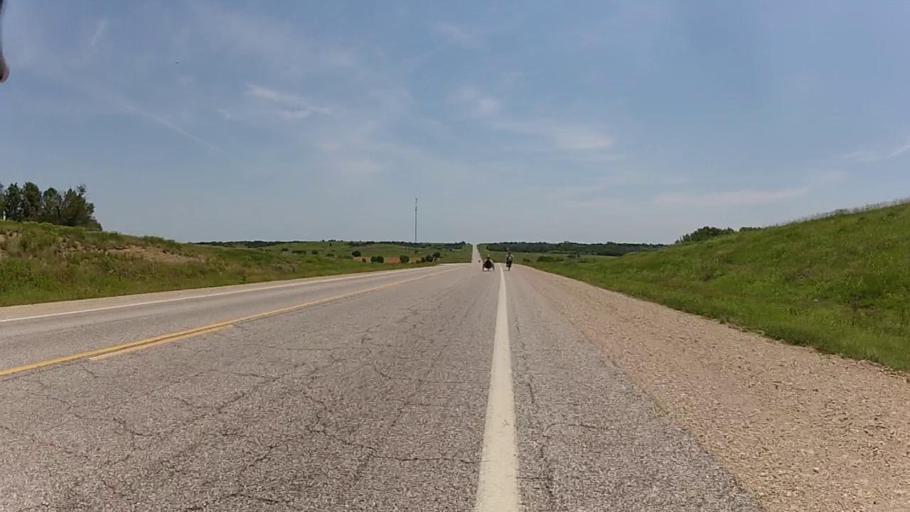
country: US
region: Kansas
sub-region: Chautauqua County
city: Sedan
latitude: 37.1133
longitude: -96.4635
